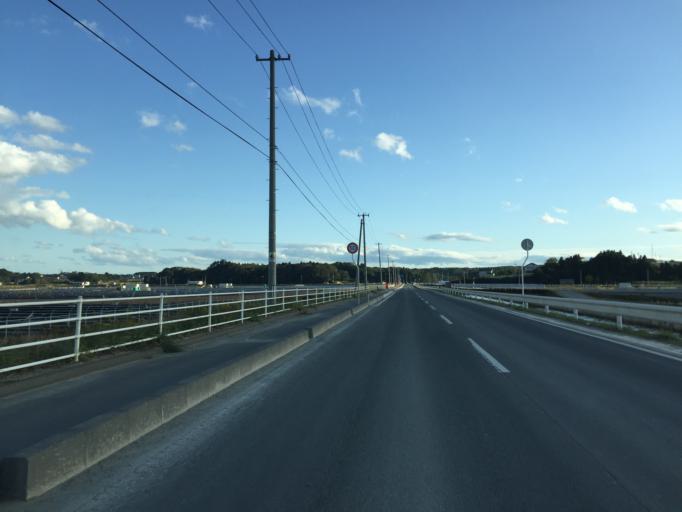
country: JP
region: Miyagi
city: Marumori
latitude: 37.7724
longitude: 140.9813
